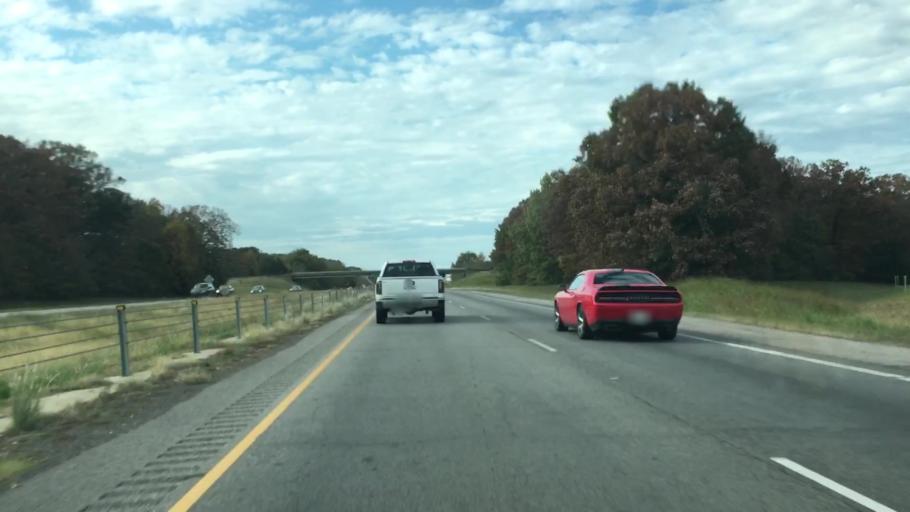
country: US
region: Arkansas
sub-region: Conway County
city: Morrilton
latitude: 35.2175
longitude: -92.8274
